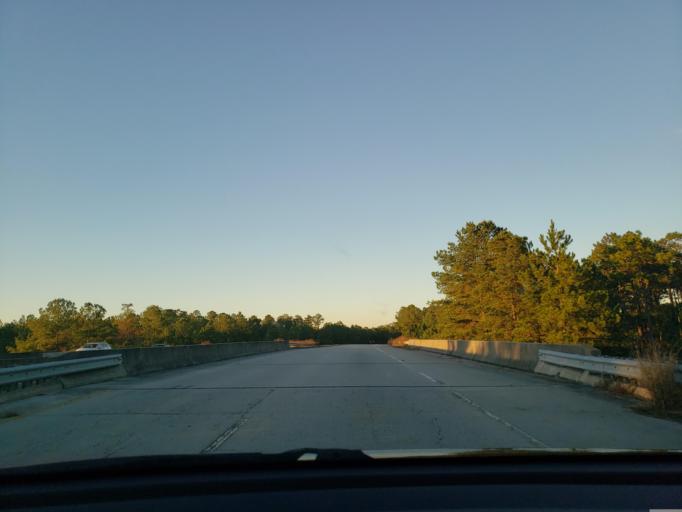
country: US
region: North Carolina
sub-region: Onslow County
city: Sneads Ferry
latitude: 34.6142
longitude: -77.4840
